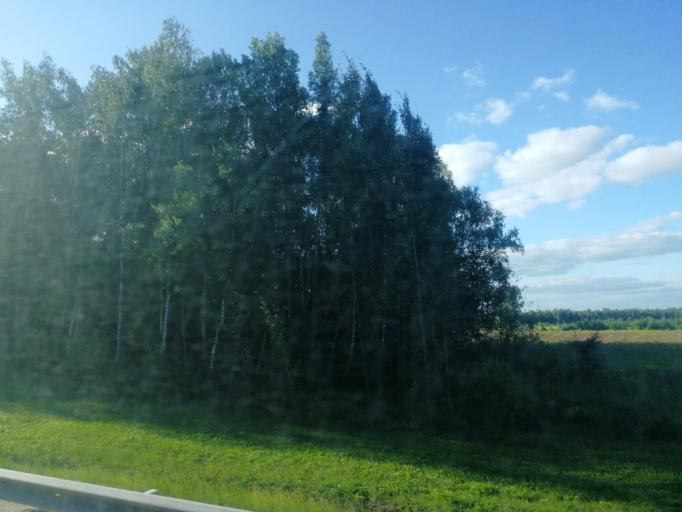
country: RU
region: Tula
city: Novogurovskiy
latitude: 54.2794
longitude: 37.2277
